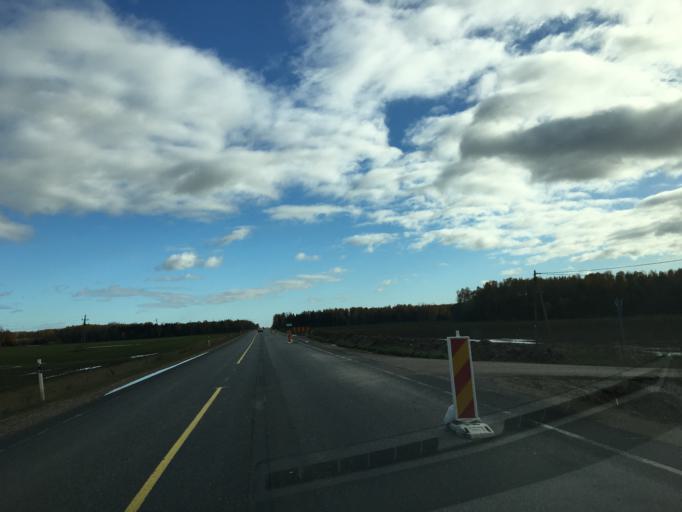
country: EE
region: Tartu
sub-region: Puhja vald
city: Puhja
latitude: 58.4648
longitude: 26.3800
